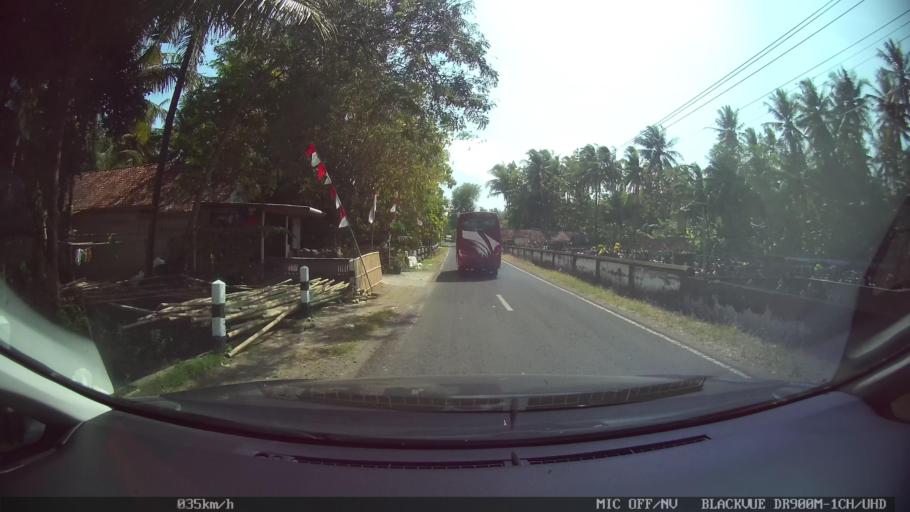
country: ID
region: Daerah Istimewa Yogyakarta
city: Srandakan
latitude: -7.9254
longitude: 110.1567
